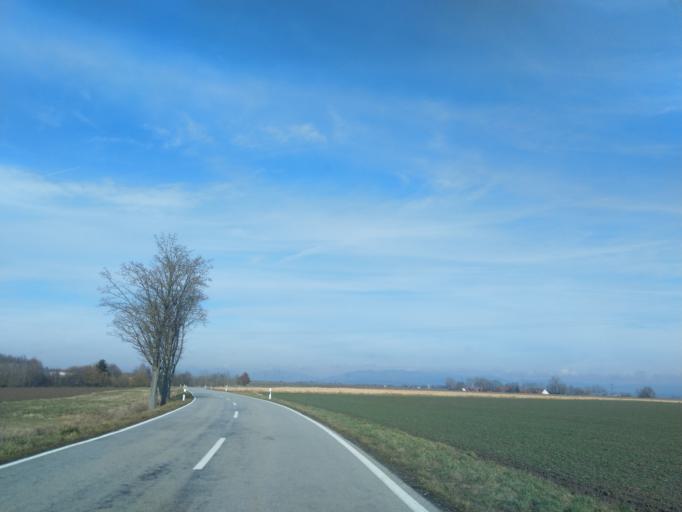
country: DE
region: Bavaria
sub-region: Lower Bavaria
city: Buchhofen
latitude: 48.6731
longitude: 12.9635
